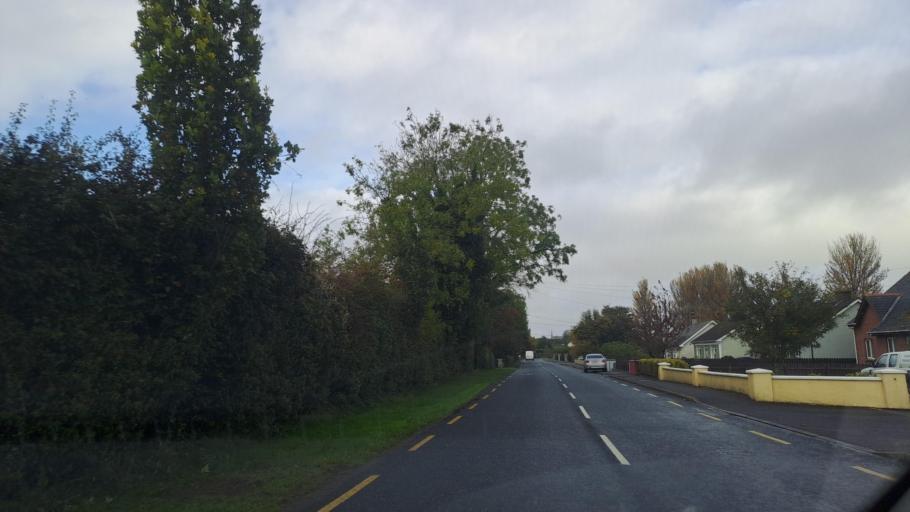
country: IE
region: Ulster
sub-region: County Monaghan
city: Carrickmacross
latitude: 53.9590
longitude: -6.7121
